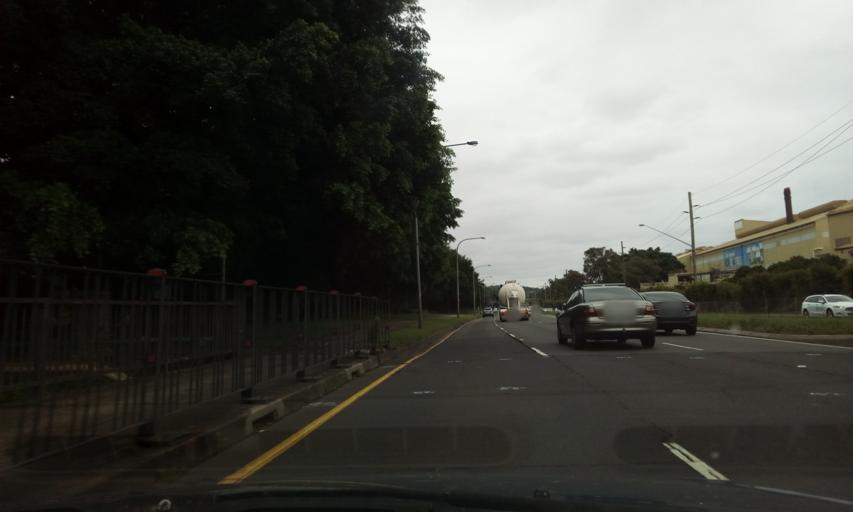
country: AU
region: New South Wales
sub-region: Wollongong
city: Cringila
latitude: -34.4610
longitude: 150.8722
